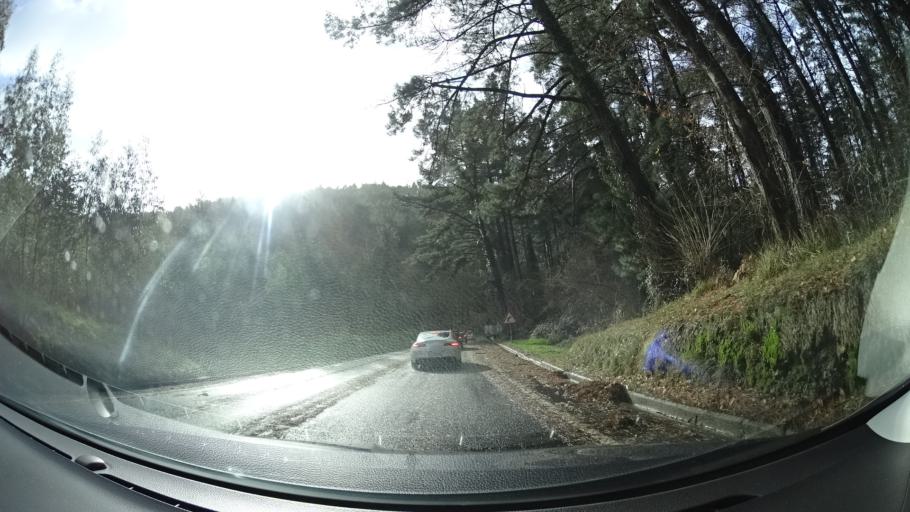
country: ES
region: Basque Country
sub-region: Bizkaia
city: Bakio
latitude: 43.3877
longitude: -2.7817
